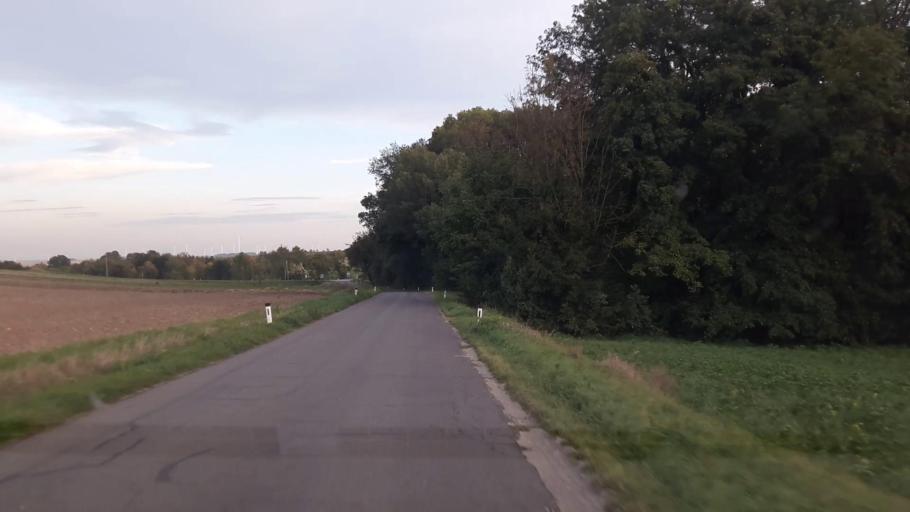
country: AT
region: Lower Austria
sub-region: Politischer Bezirk Korneuburg
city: Ernstbrunn
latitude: 48.5404
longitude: 16.3588
